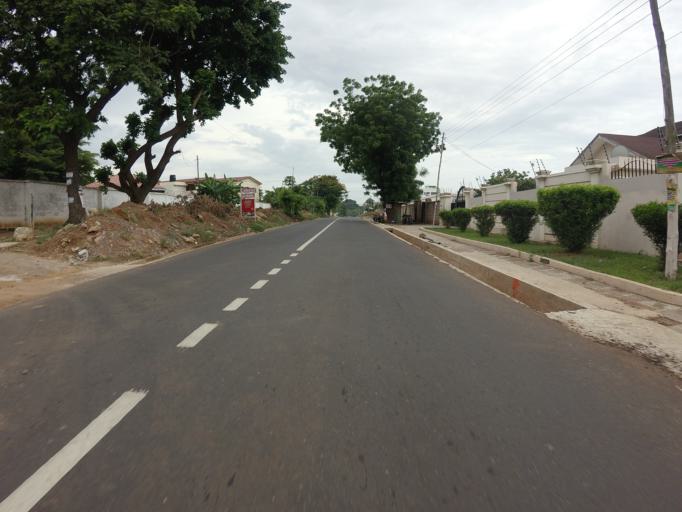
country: GH
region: Greater Accra
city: Dome
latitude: 5.6145
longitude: -0.2055
